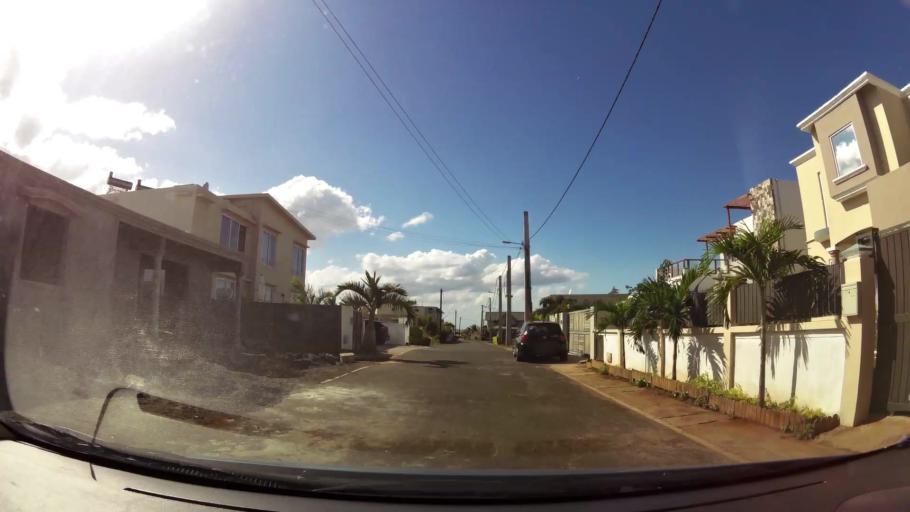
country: MU
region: Black River
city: Albion
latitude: -20.2226
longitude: 57.4134
